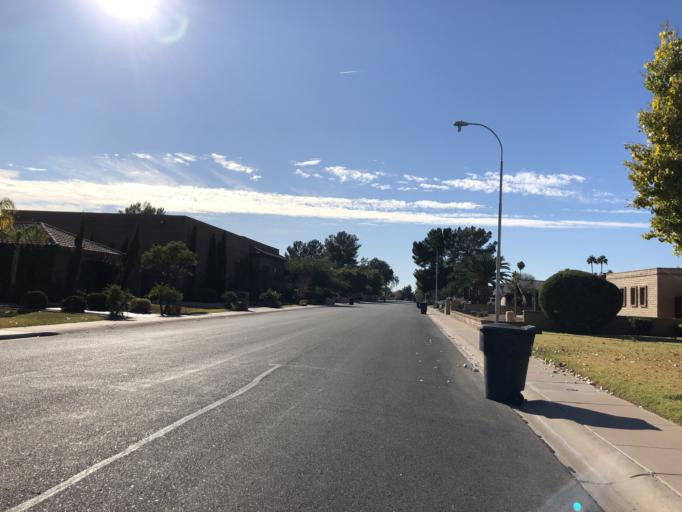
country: US
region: Arizona
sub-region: Maricopa County
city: Chandler
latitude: 33.3033
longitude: -111.9189
